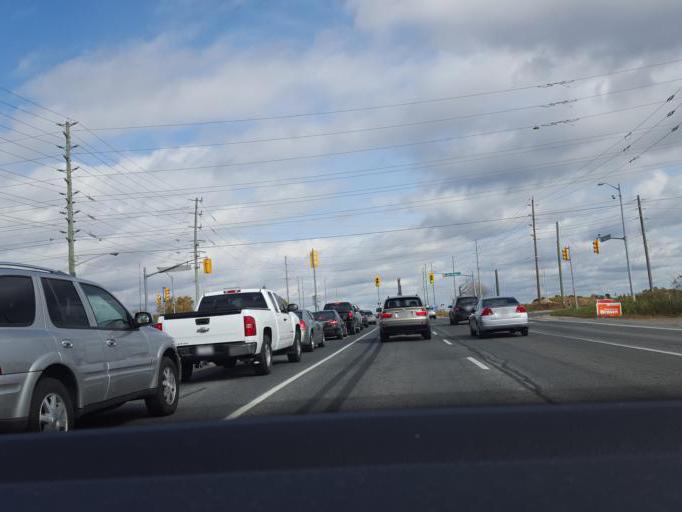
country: CA
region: Ontario
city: Ajax
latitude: 43.9048
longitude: -79.0021
